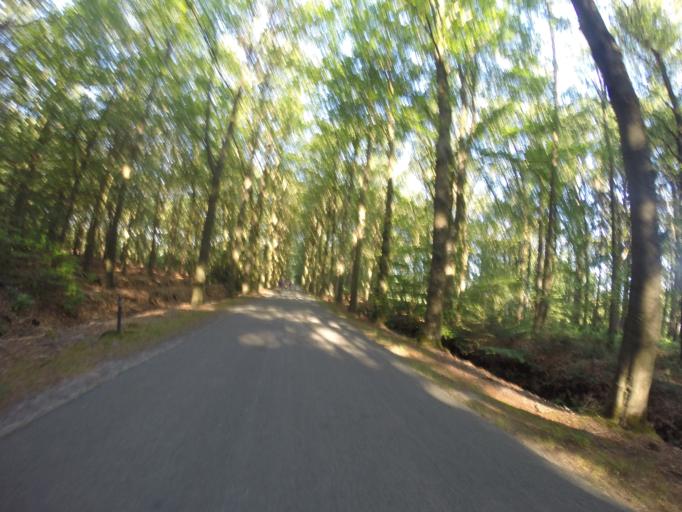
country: NL
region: Gelderland
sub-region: Gemeente Lochem
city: Barchem
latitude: 52.0929
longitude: 6.3793
